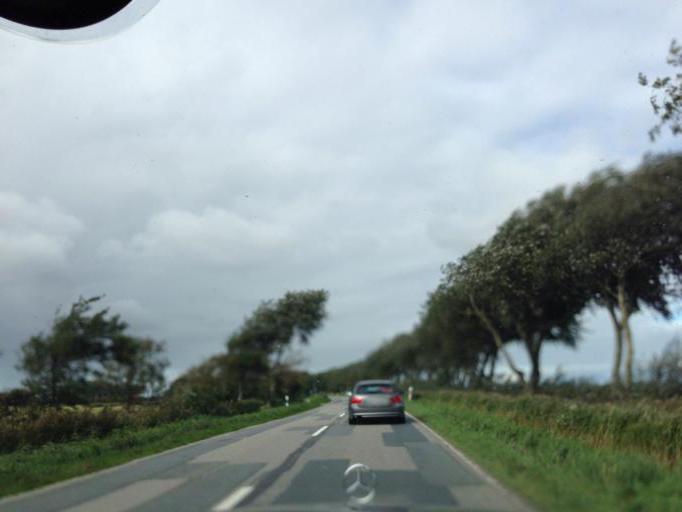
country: DE
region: Schleswig-Holstein
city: Galmsbull
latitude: 54.7639
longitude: 8.7520
